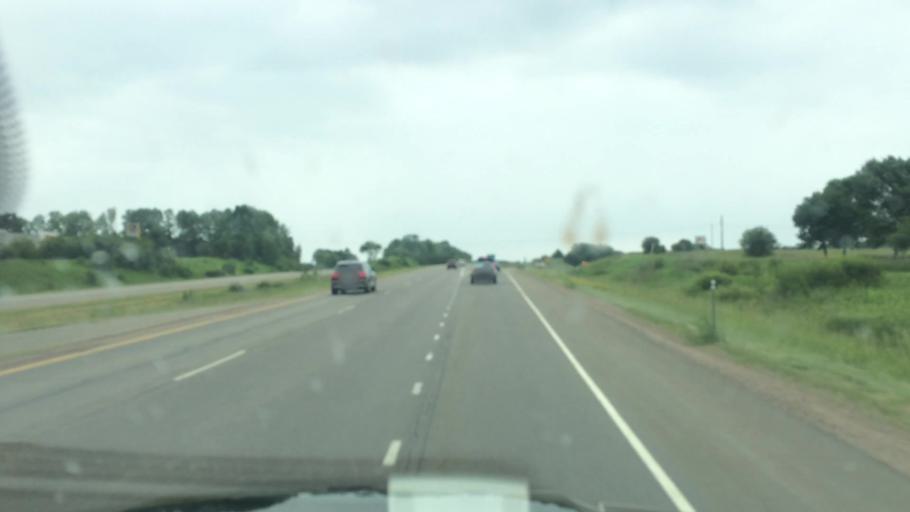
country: US
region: Wisconsin
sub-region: Lincoln County
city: Merrill
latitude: 45.1717
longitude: -89.6455
